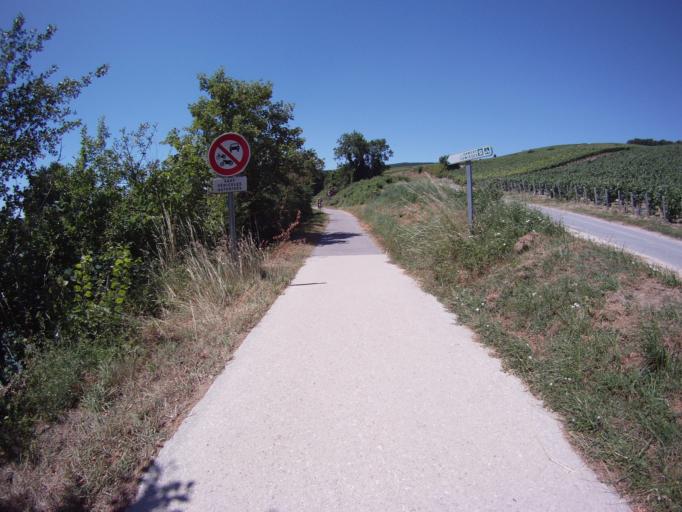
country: FR
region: Champagne-Ardenne
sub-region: Departement de la Marne
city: Mardeuil
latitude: 49.0725
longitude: 3.9408
